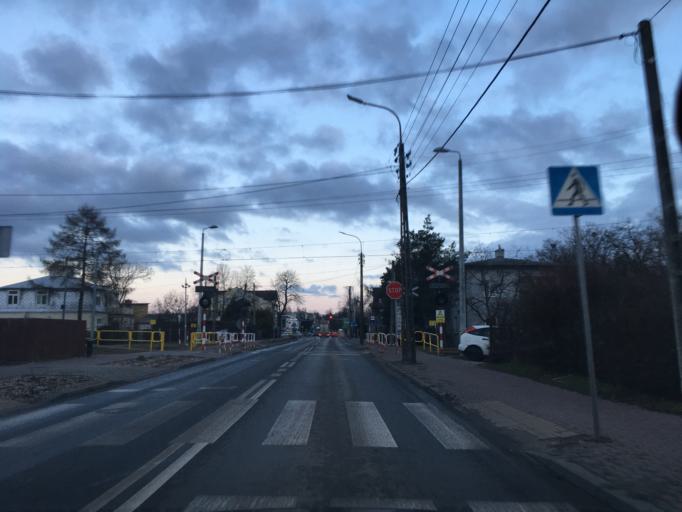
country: PL
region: Masovian Voivodeship
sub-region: Powiat grodziski
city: Grodzisk Mazowiecki
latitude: 52.1031
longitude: 20.6372
